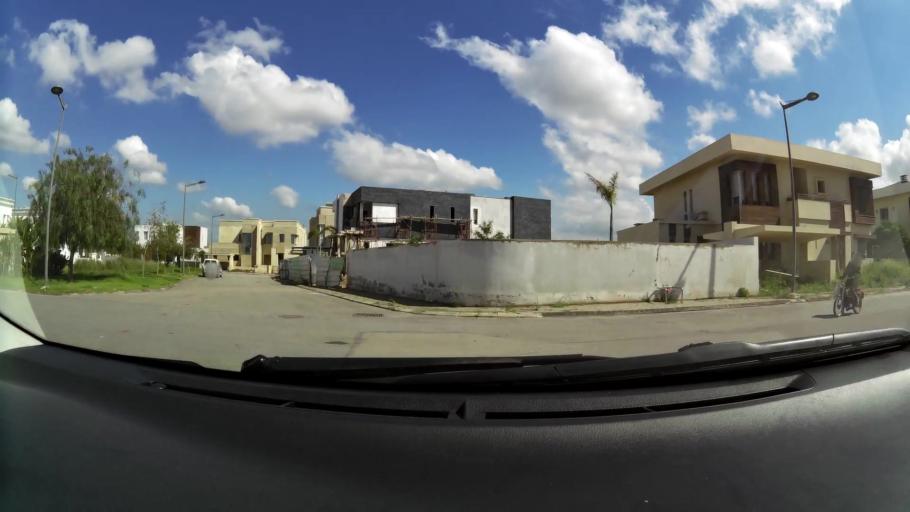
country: MA
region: Grand Casablanca
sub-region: Nouaceur
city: Bouskoura
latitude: 33.4667
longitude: -7.5951
